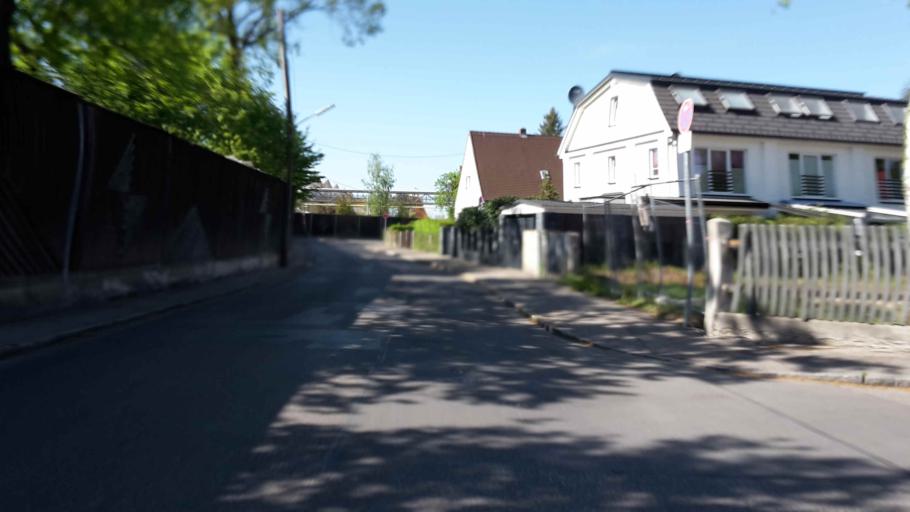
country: DE
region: Bavaria
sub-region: Upper Bavaria
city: Karlsfeld
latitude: 48.1878
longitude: 11.4723
